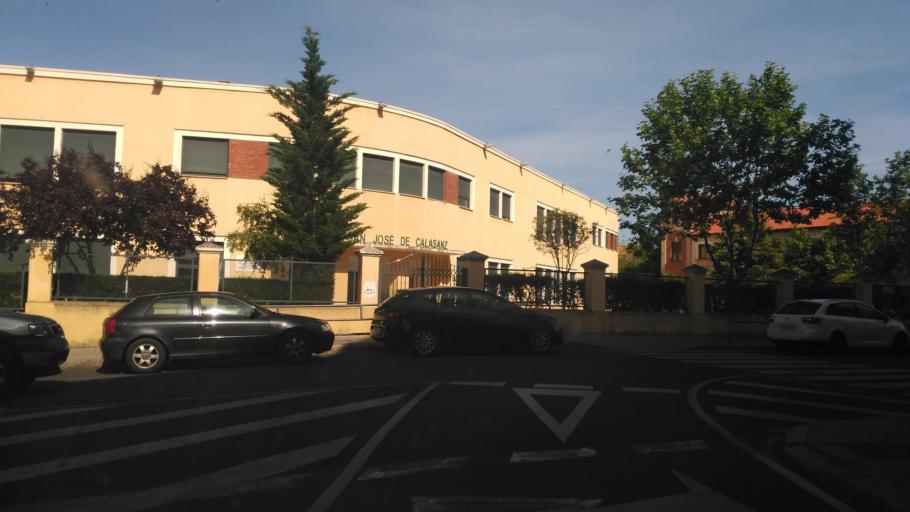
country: ES
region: Castille and Leon
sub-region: Provincia de Zamora
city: Zamora
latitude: 41.5083
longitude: -5.7441
